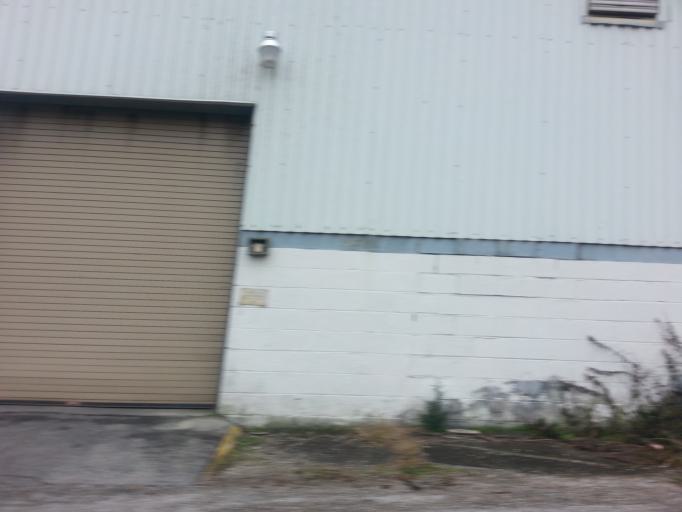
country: US
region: Tennessee
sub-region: Jefferson County
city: Jefferson City
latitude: 36.1257
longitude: -83.4939
